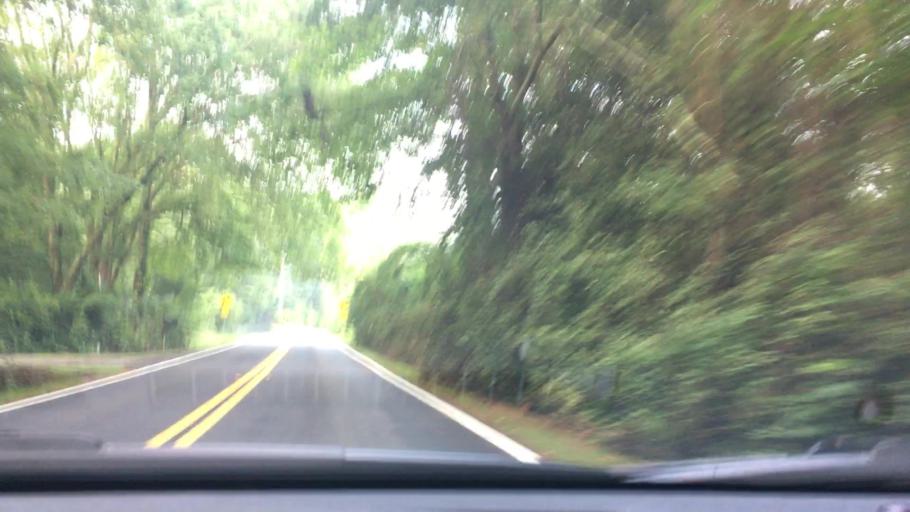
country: US
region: Georgia
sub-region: Cobb County
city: Marietta
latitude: 33.9795
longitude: -84.5882
